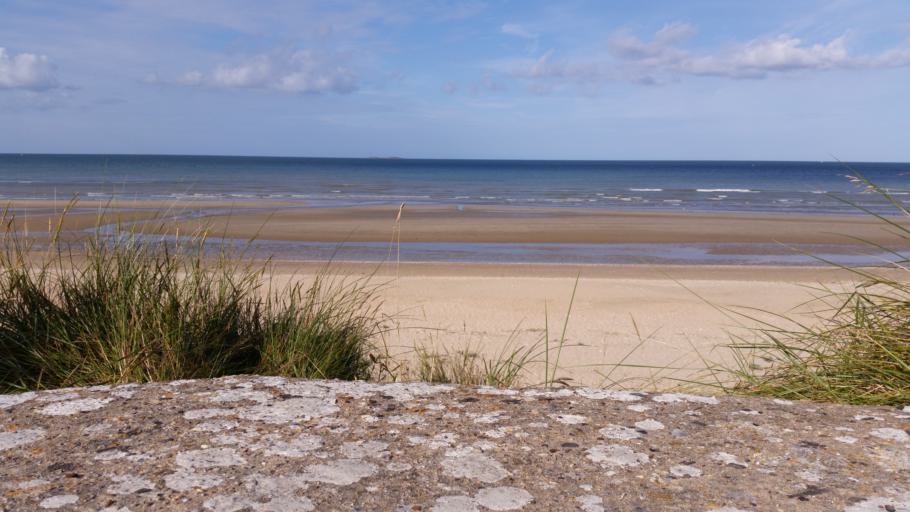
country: FR
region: Lower Normandy
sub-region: Departement de la Manche
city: Sainte-Mere-Eglise
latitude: 49.4453
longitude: -1.2099
